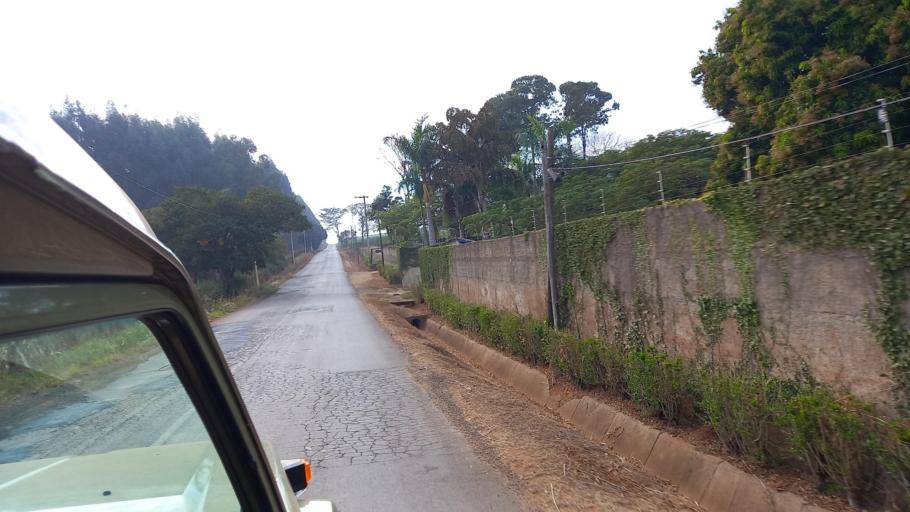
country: BR
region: Sao Paulo
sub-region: Moji-Guacu
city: Mogi-Gaucu
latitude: -22.3316
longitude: -46.8781
